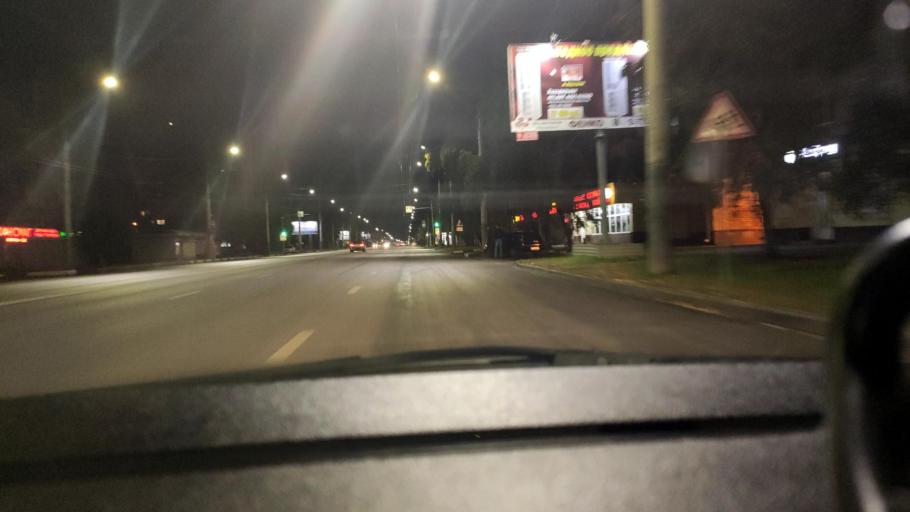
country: RU
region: Voronezj
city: Voronezh
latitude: 51.6512
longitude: 39.2419
